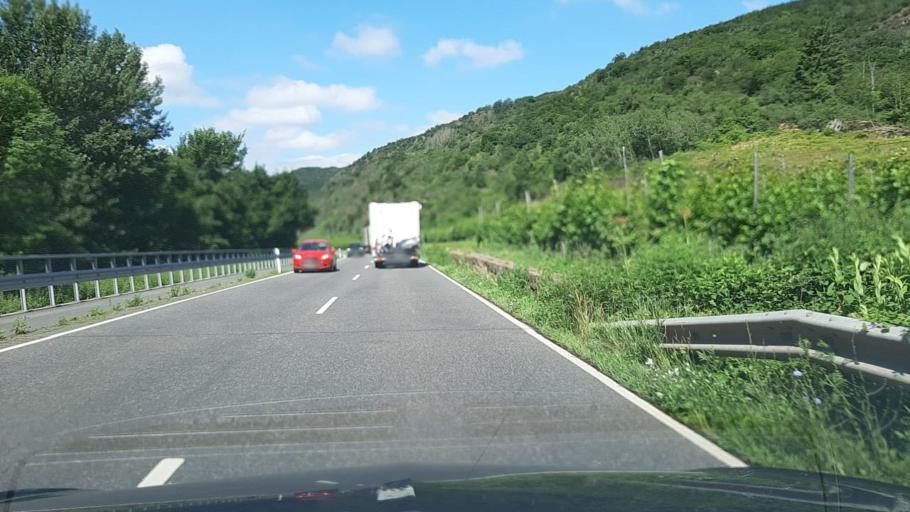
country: DE
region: Rheinland-Pfalz
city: Kail
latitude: 50.1687
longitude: 7.2474
